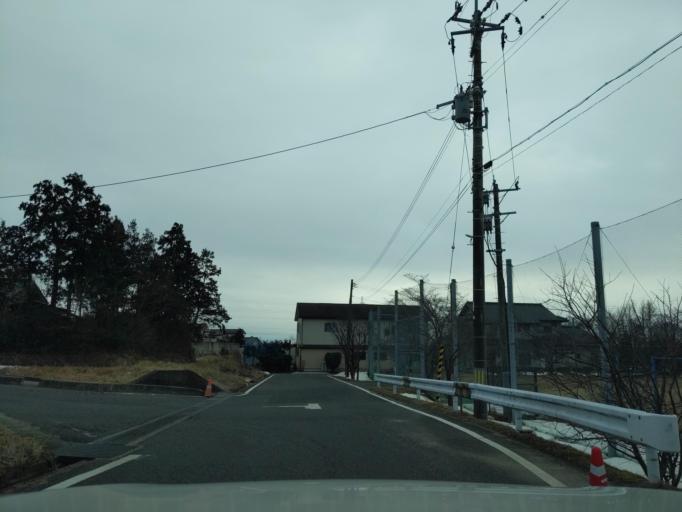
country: JP
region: Fukushima
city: Koriyama
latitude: 37.4544
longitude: 140.3848
